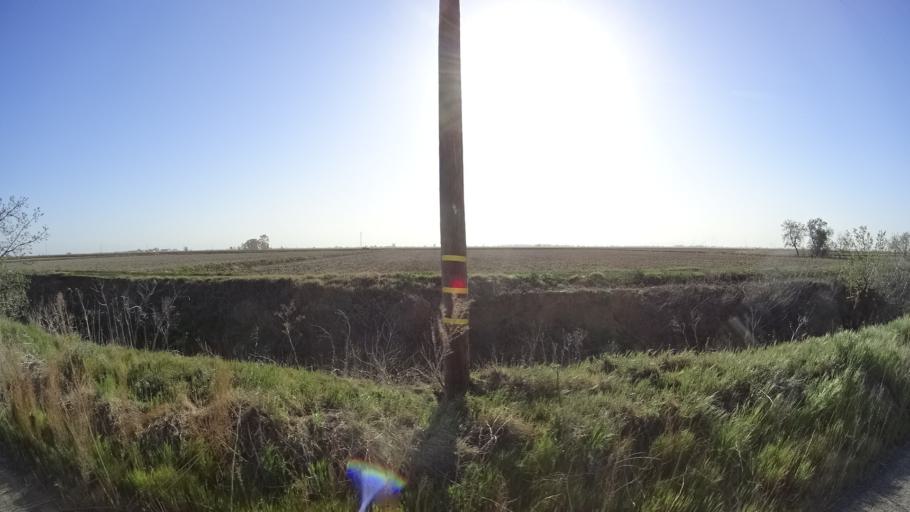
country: US
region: California
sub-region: Glenn County
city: Willows
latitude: 39.4042
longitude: -122.2300
